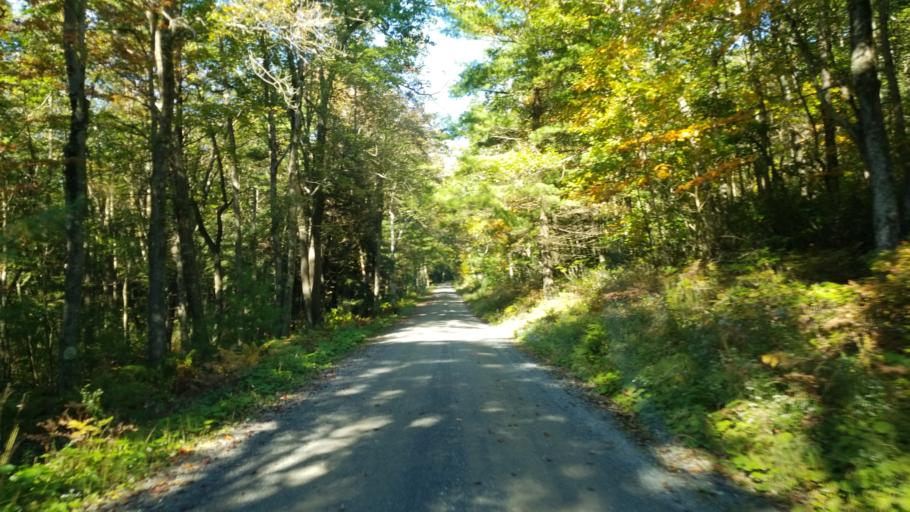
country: US
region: Pennsylvania
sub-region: Clearfield County
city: Hyde
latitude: 41.0854
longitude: -78.5287
